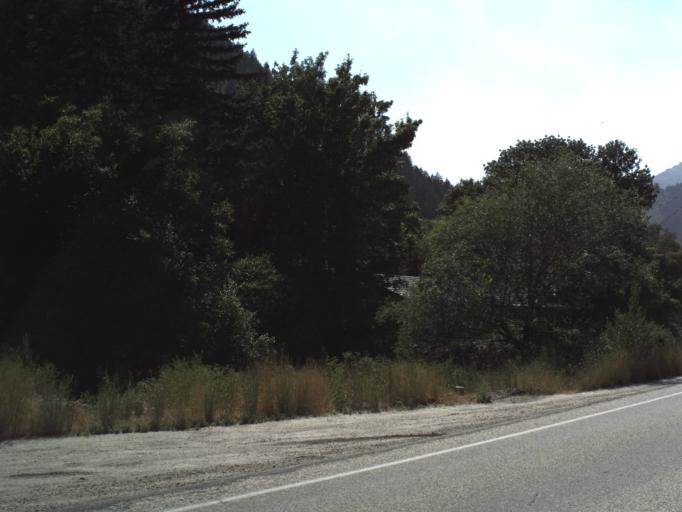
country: US
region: Utah
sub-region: Weber County
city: Liberty
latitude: 41.2538
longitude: -111.8519
